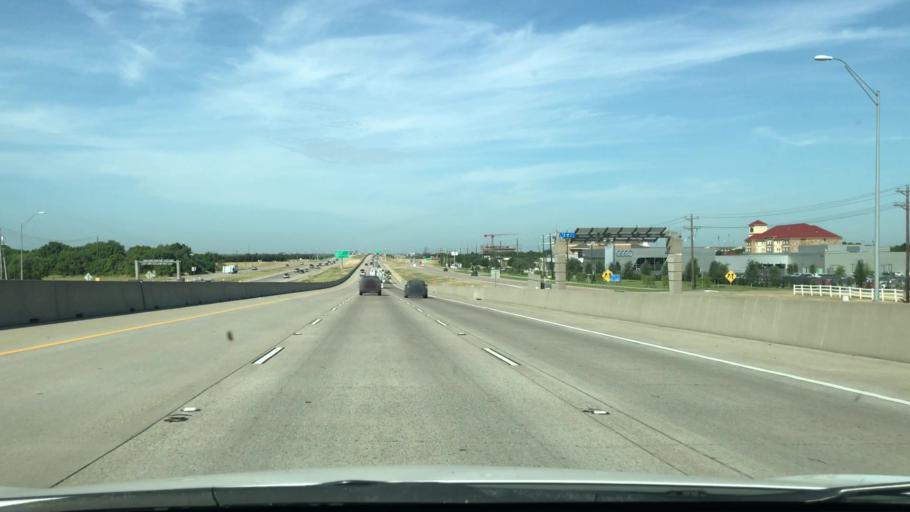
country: US
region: Texas
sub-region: Collin County
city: Allen
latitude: 33.1389
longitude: -96.6949
